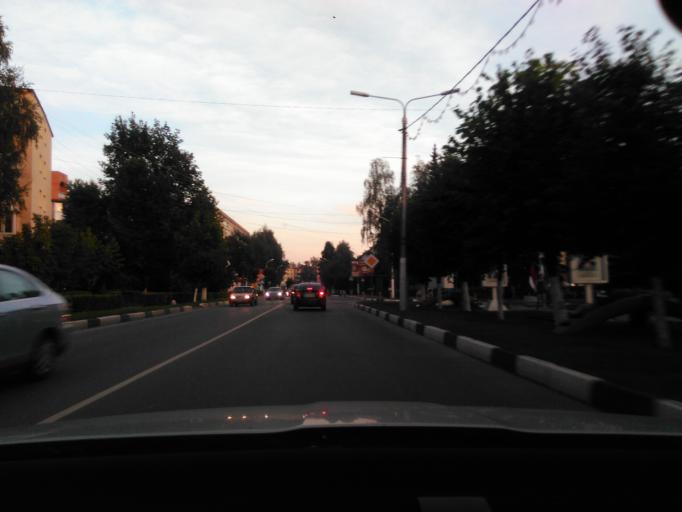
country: RU
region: Moskovskaya
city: Klin
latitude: 56.3224
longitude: 36.7210
